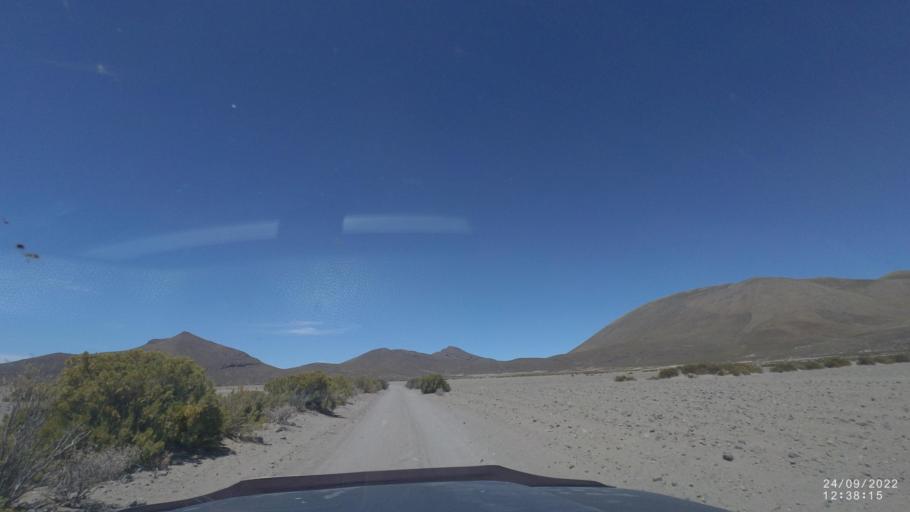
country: BO
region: Potosi
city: Colchani
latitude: -19.7888
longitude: -67.5862
